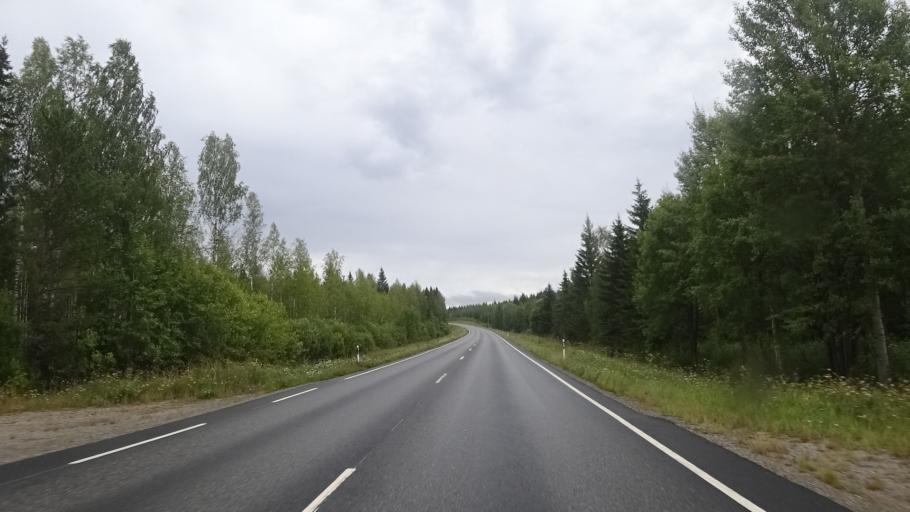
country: FI
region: Southern Savonia
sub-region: Savonlinna
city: Kerimaeki
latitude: 62.0075
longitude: 29.3287
